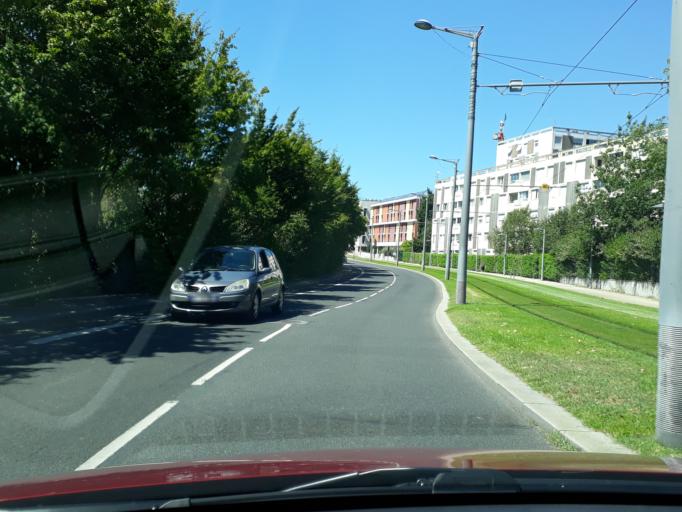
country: FR
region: Rhone-Alpes
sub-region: Departement du Rhone
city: Saint-Priest
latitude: 45.6927
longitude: 4.9532
